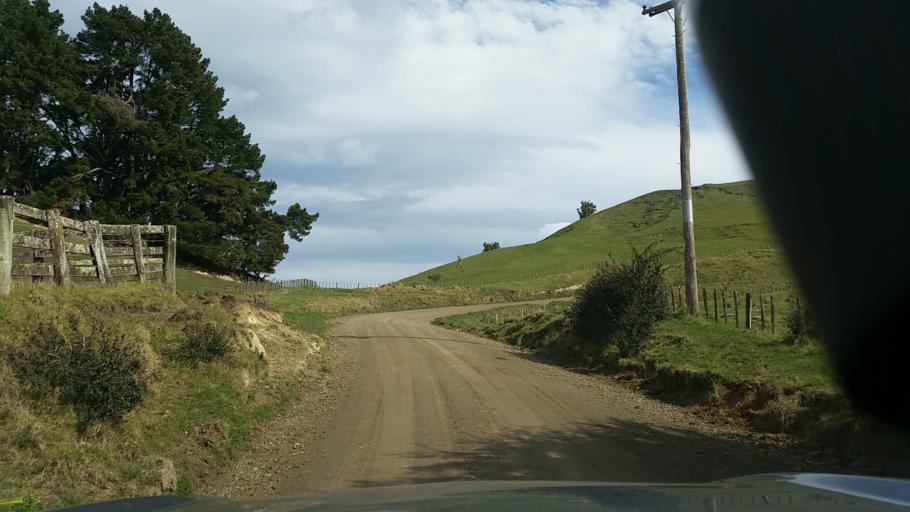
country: NZ
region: Hawke's Bay
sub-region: Napier City
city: Napier
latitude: -39.2114
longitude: 176.9675
